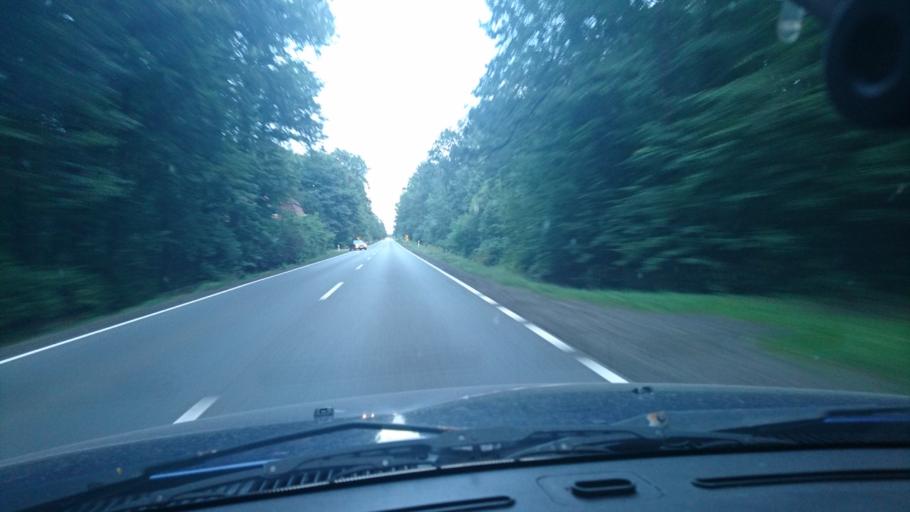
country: PL
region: Silesian Voivodeship
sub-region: Powiat tarnogorski
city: Tworog
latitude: 50.5114
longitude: 18.7446
